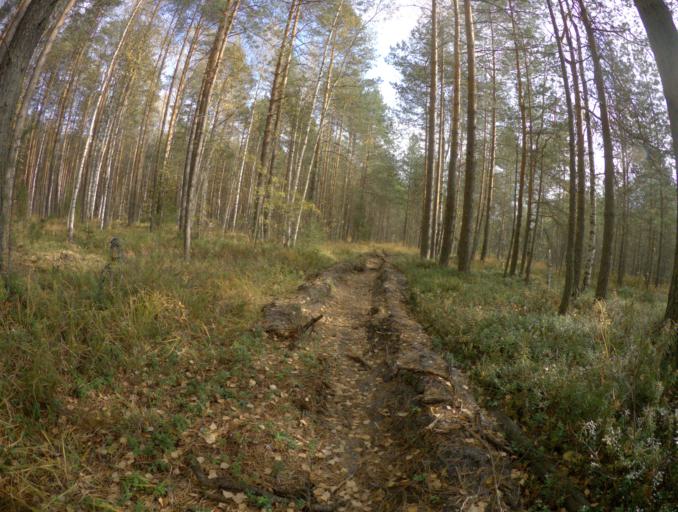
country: RU
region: Vladimir
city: Raduzhnyy
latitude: 55.9386
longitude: 40.3286
